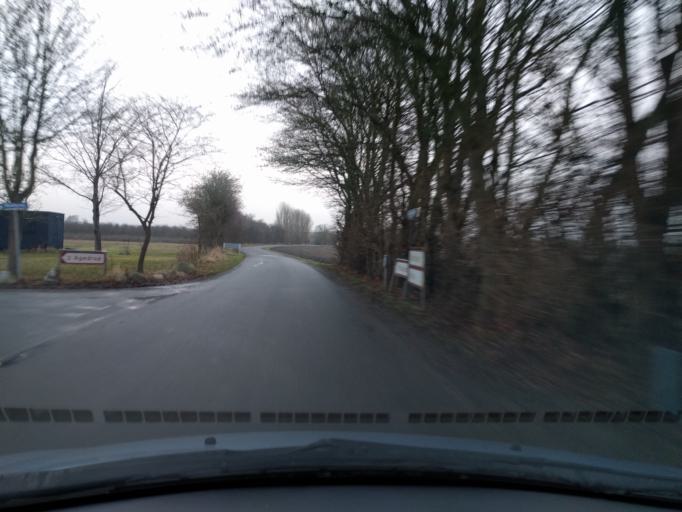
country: DK
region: South Denmark
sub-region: Odense Kommune
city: Bullerup
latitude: 55.4192
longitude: 10.5235
